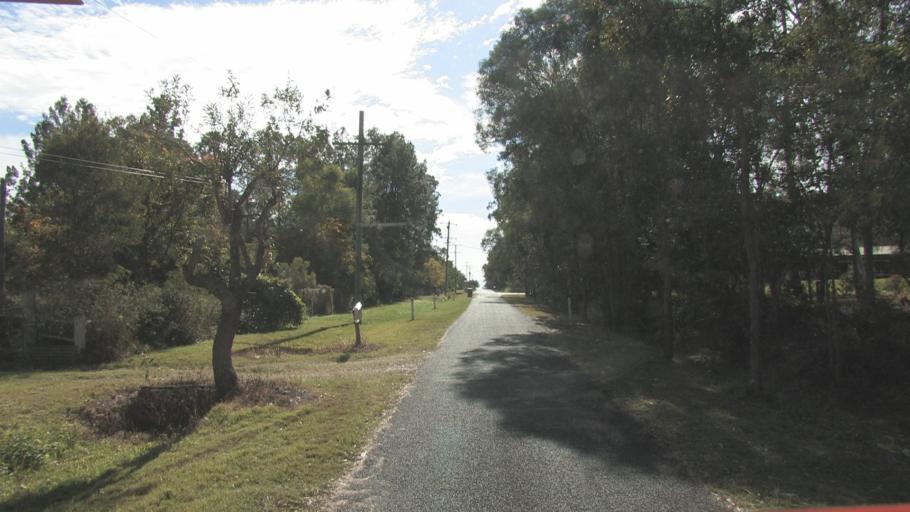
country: AU
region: Queensland
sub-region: Logan
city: North Maclean
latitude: -27.7806
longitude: 152.9904
